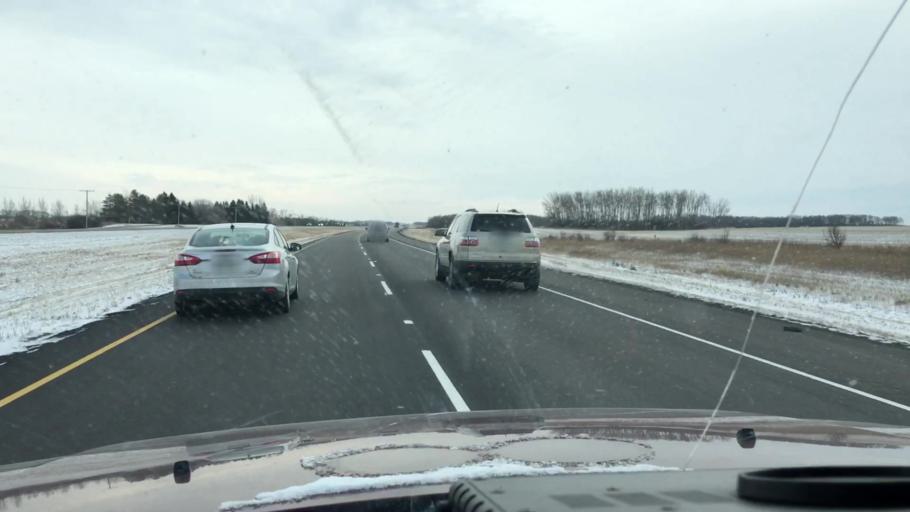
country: CA
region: Saskatchewan
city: Saskatoon
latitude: 52.0177
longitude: -106.5765
